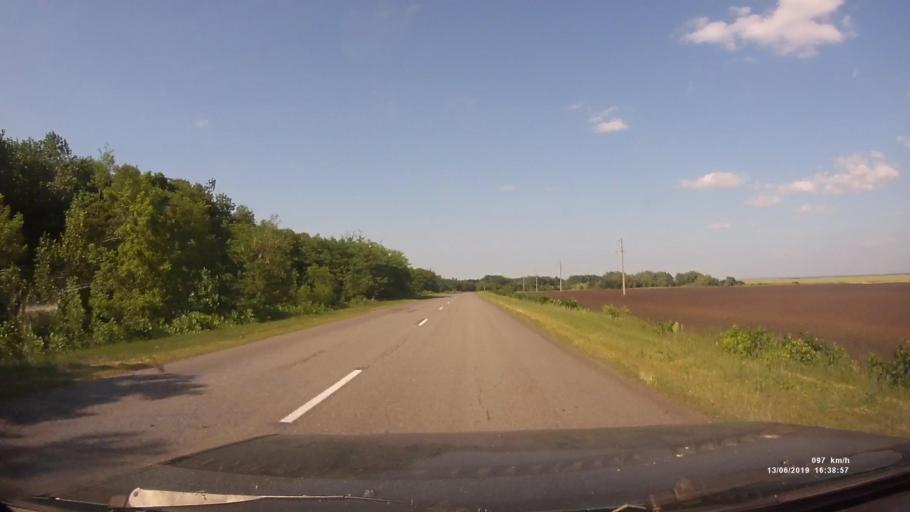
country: RU
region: Rostov
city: Kazanskaya
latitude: 49.9240
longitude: 41.3317
